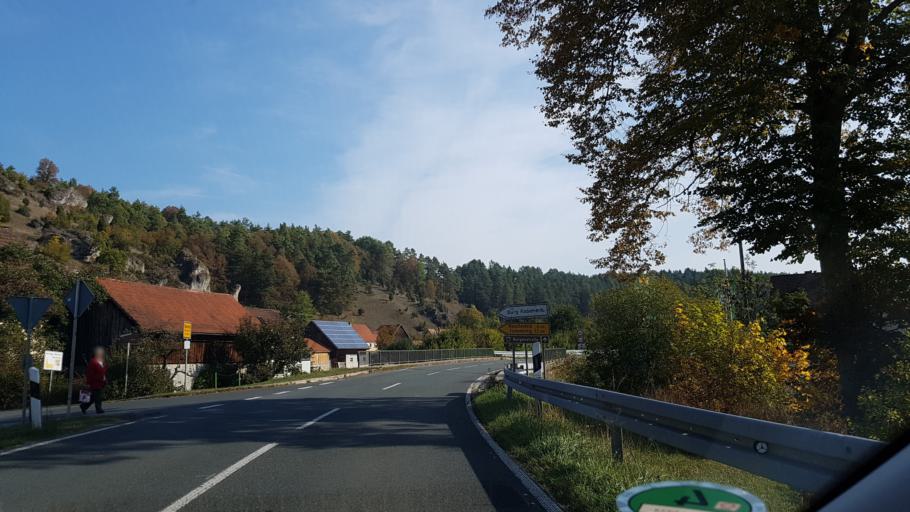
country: DE
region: Bavaria
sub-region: Upper Franconia
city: Waischenfeld
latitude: 49.8118
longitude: 11.3537
